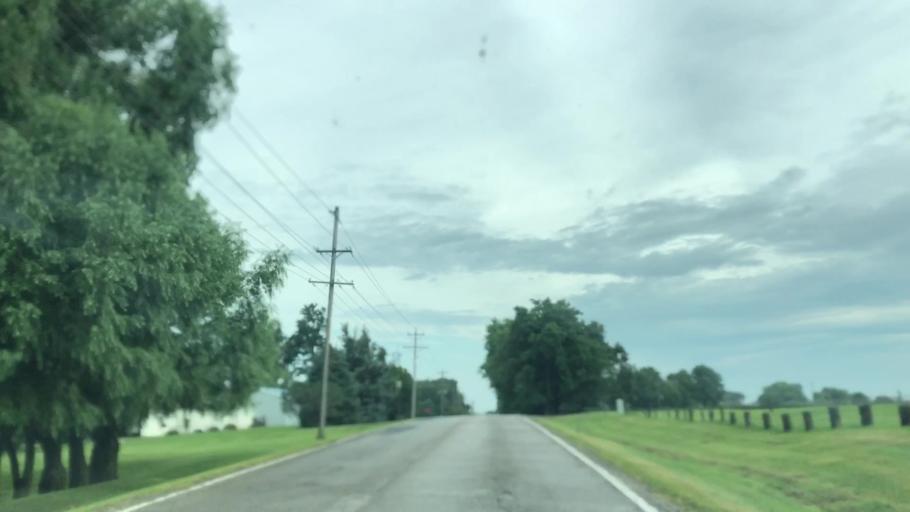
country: US
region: Iowa
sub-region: Marshall County
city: Marshalltown
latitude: 42.0431
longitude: -92.9608
